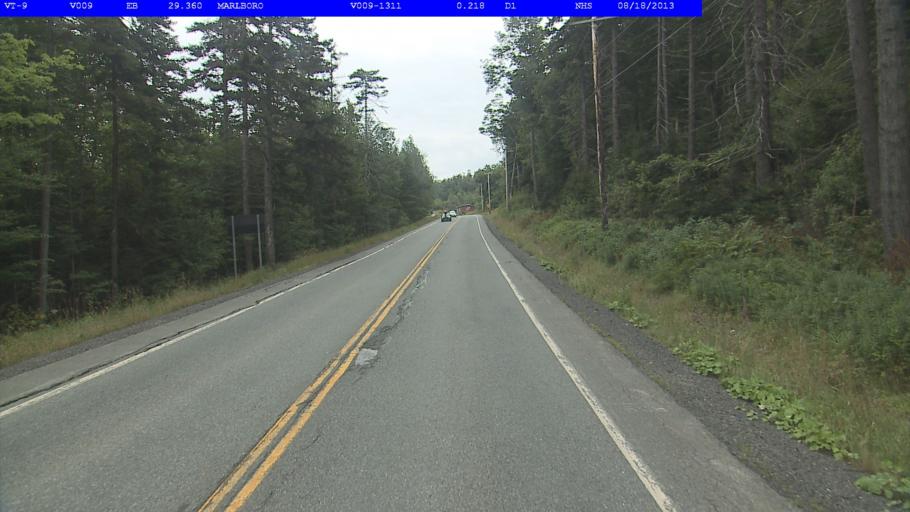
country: US
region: Vermont
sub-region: Windham County
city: Dover
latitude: 42.8569
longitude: -72.7991
